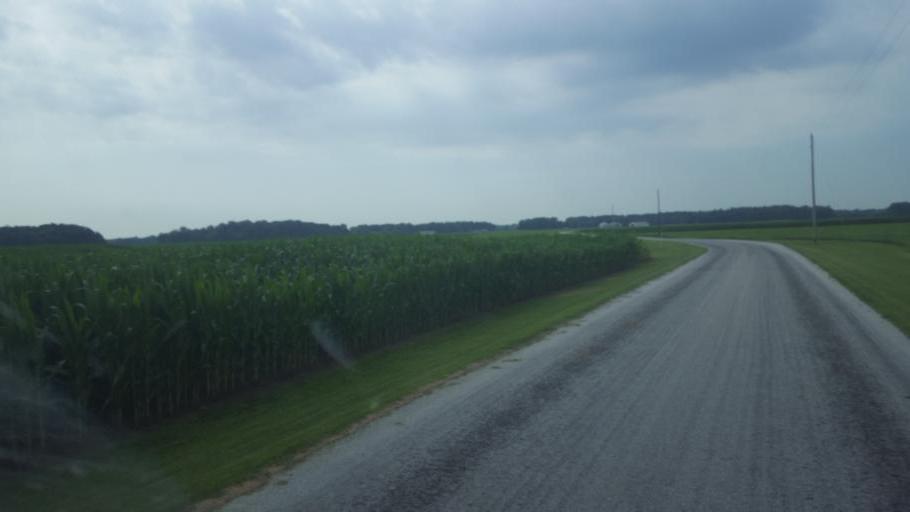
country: US
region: Ohio
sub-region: Hardin County
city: Kenton
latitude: 40.5929
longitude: -83.5227
